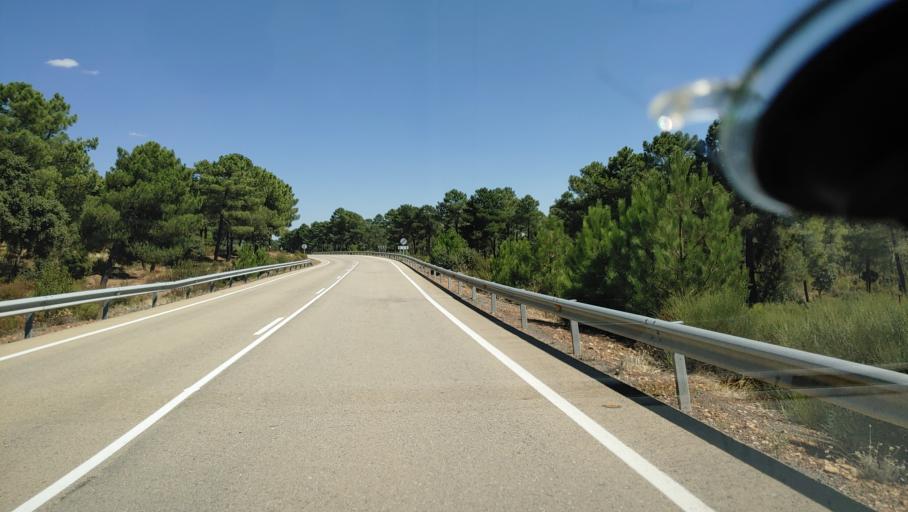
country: ES
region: Castille-La Mancha
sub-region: Provincia de Ciudad Real
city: Saceruela
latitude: 38.9919
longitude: -4.5286
